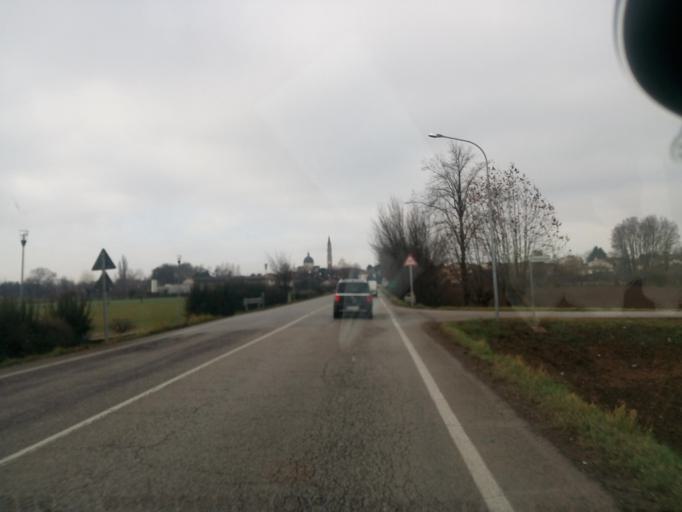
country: IT
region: Veneto
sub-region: Provincia di Vicenza
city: Sandrigo
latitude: 45.6616
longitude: 11.6121
